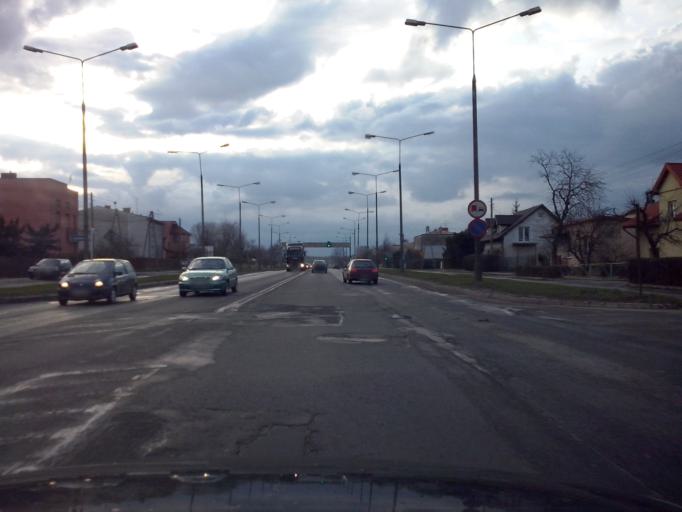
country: PL
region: Lublin Voivodeship
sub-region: Chelm
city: Chelm
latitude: 51.1450
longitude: 23.4532
